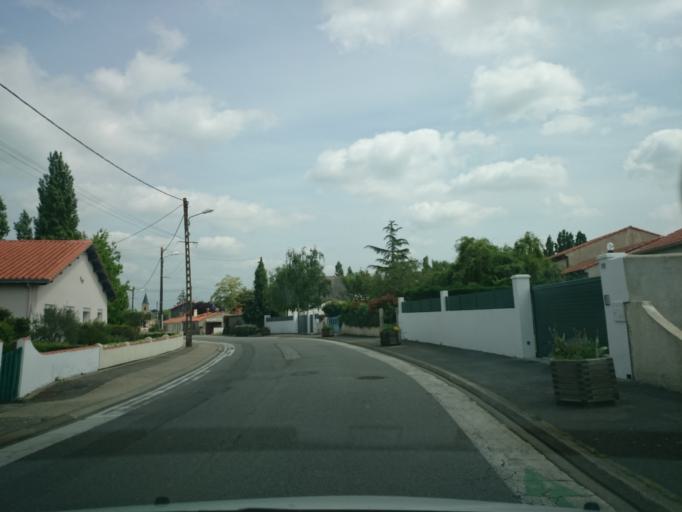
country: FR
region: Pays de la Loire
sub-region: Departement de la Loire-Atlantique
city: La Chevroliere
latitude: 47.1232
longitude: -1.6377
